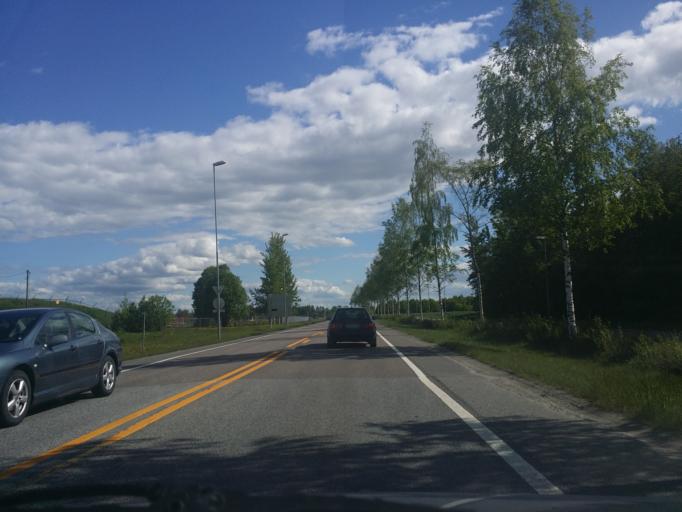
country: NO
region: Akershus
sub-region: Nannestad
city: Teigebyen
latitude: 60.1855
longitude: 11.0679
